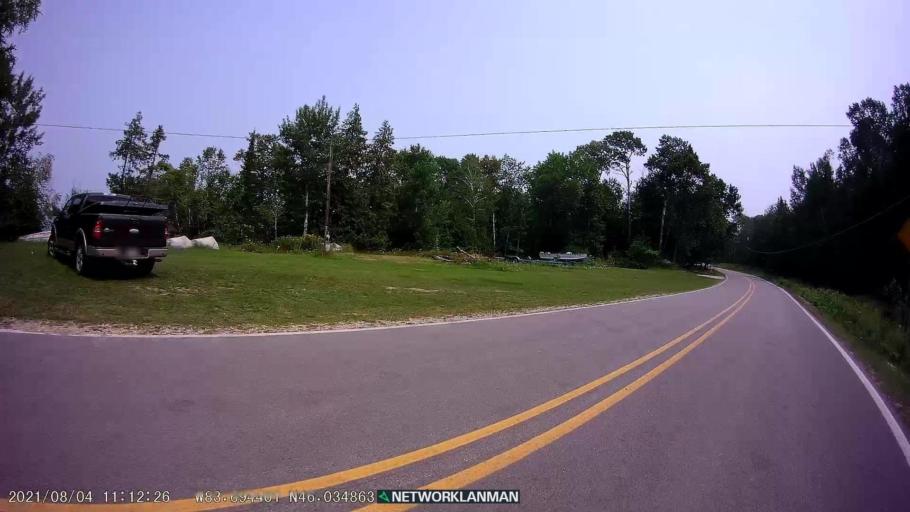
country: CA
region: Ontario
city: Thessalon
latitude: 46.0348
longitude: -83.6944
